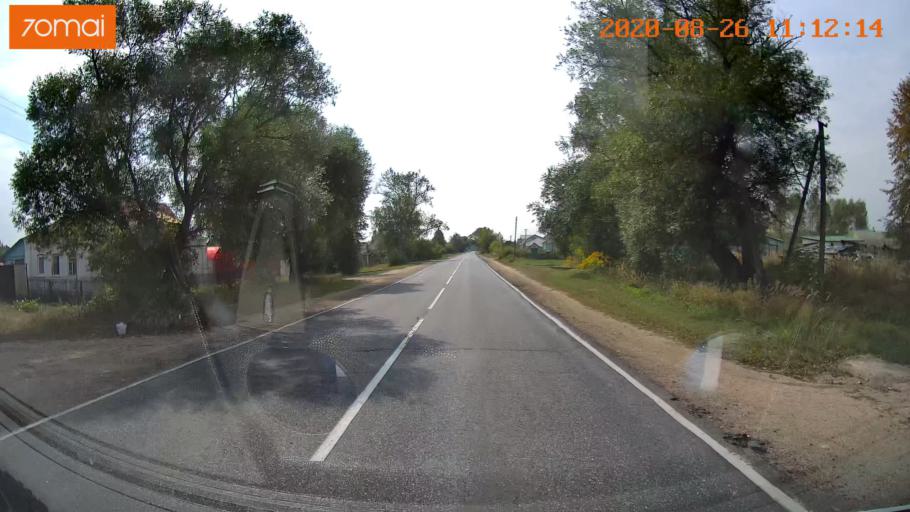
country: RU
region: Rjazan
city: Izhevskoye
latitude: 54.4725
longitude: 41.1254
